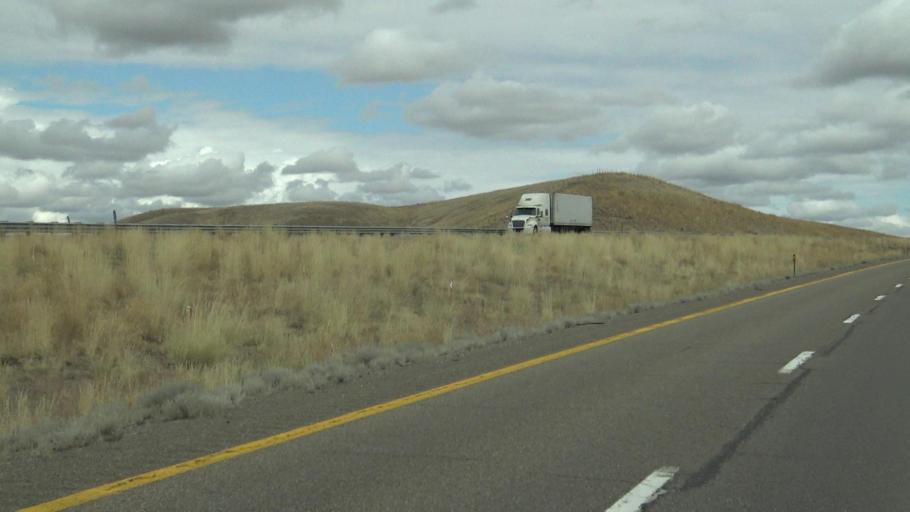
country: US
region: Nevada
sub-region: Elko County
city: Elko
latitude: 40.8935
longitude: -115.7111
